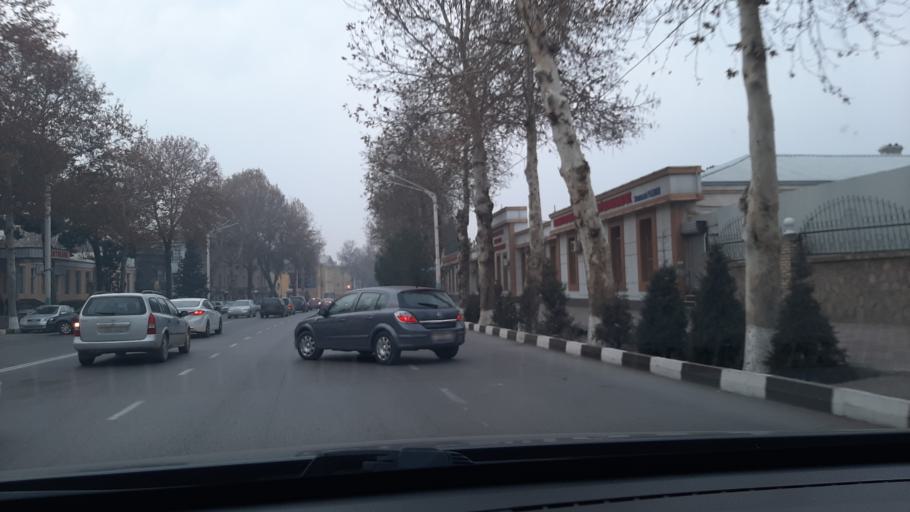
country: TJ
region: Viloyati Sughd
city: Khujand
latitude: 40.2728
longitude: 69.6409
